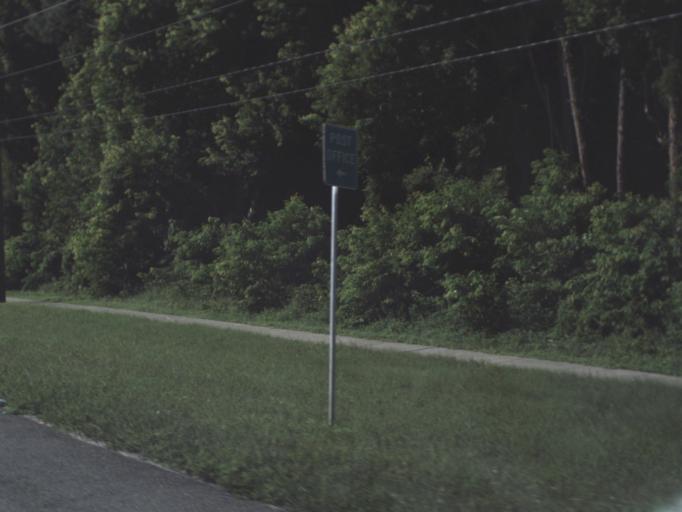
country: US
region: Florida
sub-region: Lee County
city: San Carlos Park
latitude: 26.4797
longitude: -81.8390
